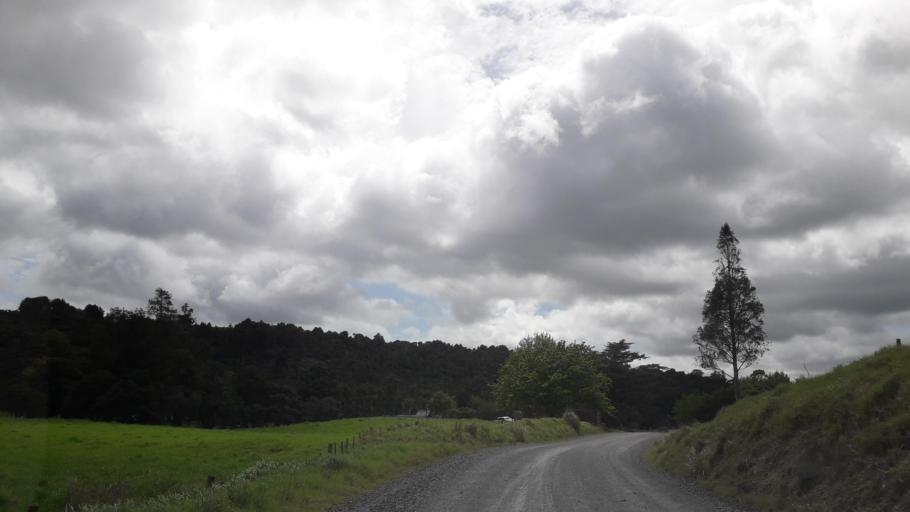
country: NZ
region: Northland
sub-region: Far North District
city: Kaitaia
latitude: -35.1730
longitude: 173.3303
